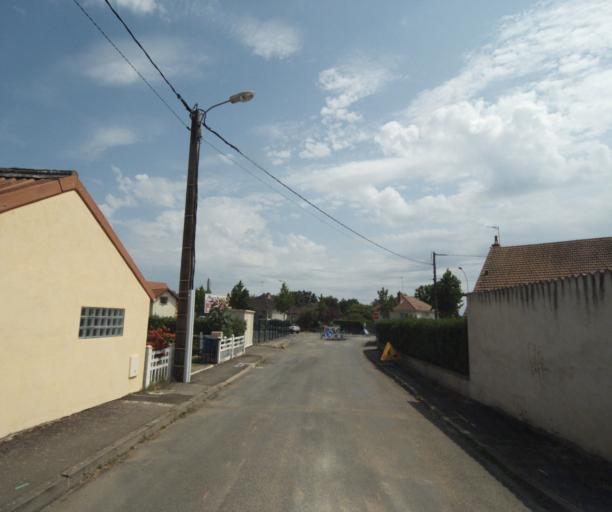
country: FR
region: Bourgogne
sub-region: Departement de Saone-et-Loire
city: Gueugnon
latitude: 46.5988
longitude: 4.0487
